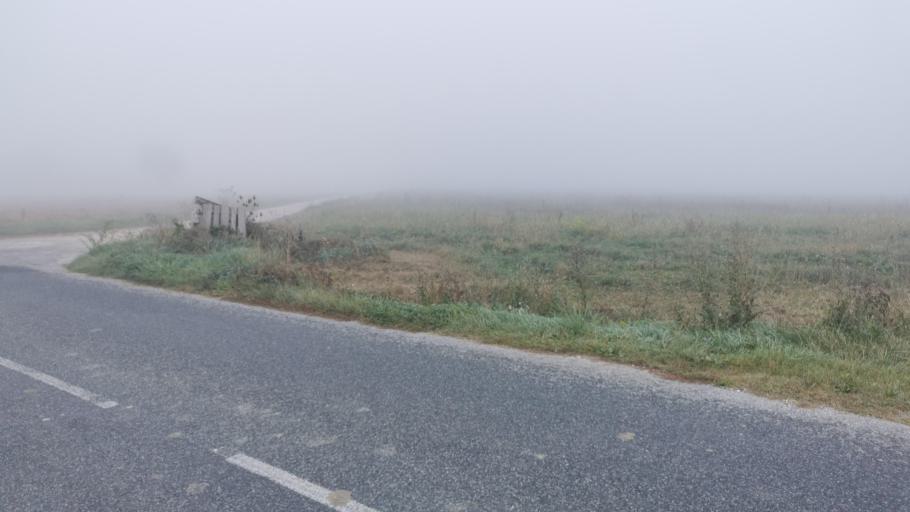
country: FR
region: Midi-Pyrenees
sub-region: Departement du Tarn
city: Dourgne
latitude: 43.4983
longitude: 2.1135
